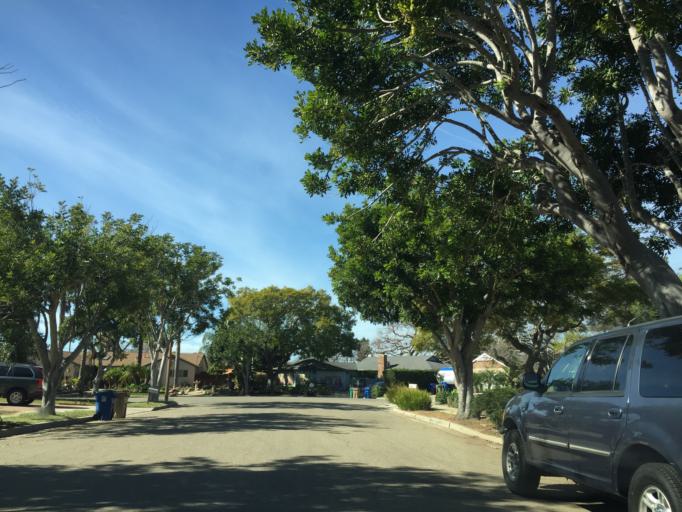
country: US
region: California
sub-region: Santa Barbara County
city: Goleta
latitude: 34.4345
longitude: -119.7850
